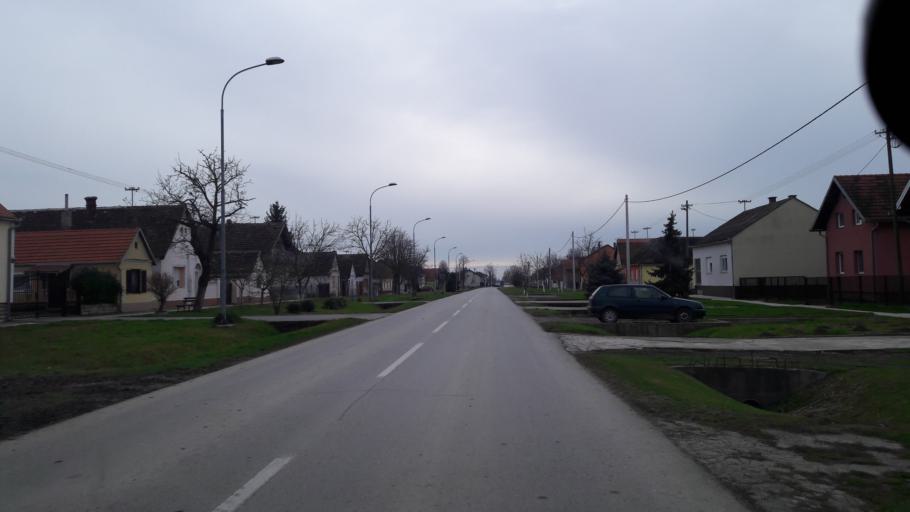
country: HR
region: Osjecko-Baranjska
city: Vladislavci
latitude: 45.4602
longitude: 18.5732
